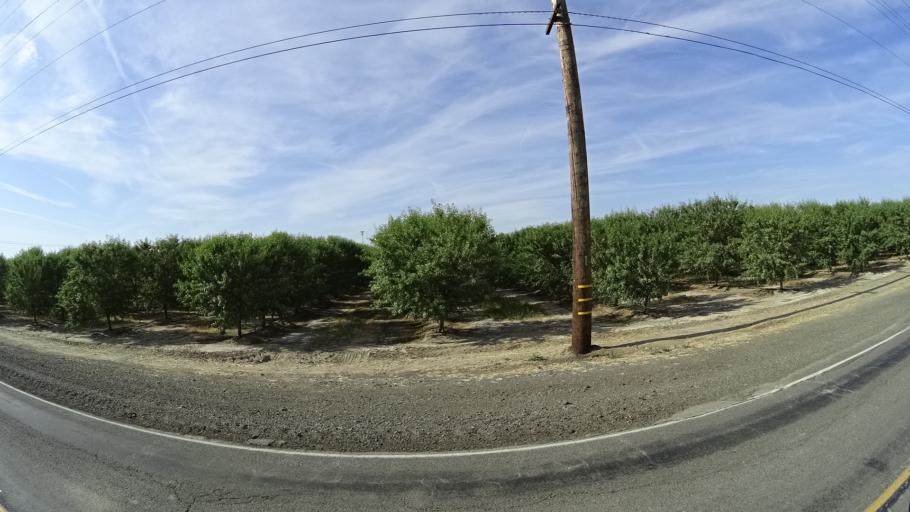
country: US
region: California
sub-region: Tulare County
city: Goshen
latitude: 36.3419
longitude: -119.4762
